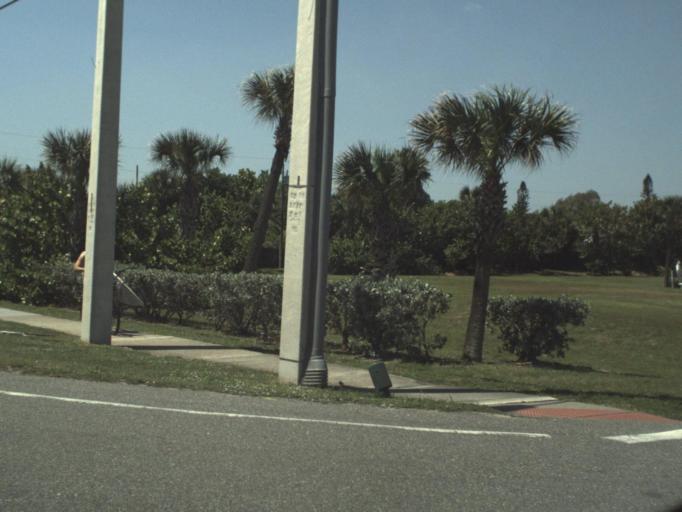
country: US
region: Florida
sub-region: Brevard County
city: Indian Harbour Beach
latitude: 28.1339
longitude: -80.5799
